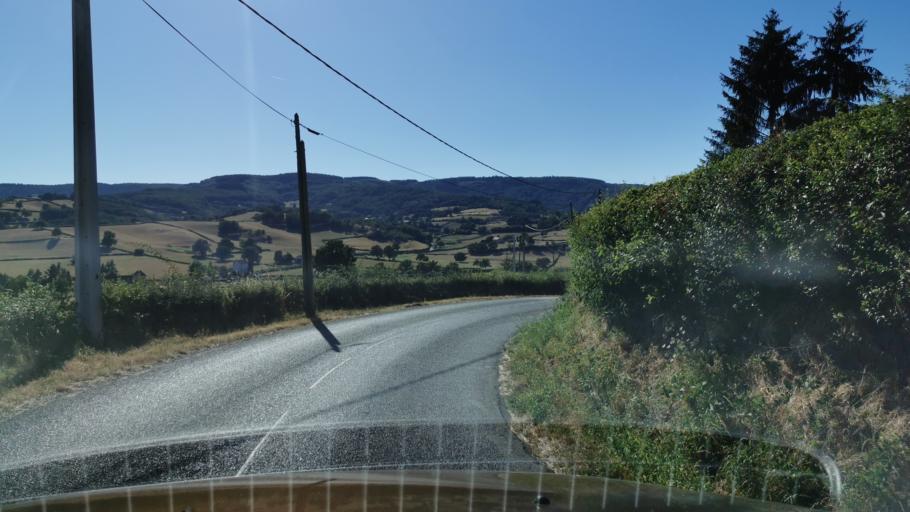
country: FR
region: Bourgogne
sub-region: Departement de Saone-et-Loire
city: Marmagne
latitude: 46.8049
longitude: 4.3376
